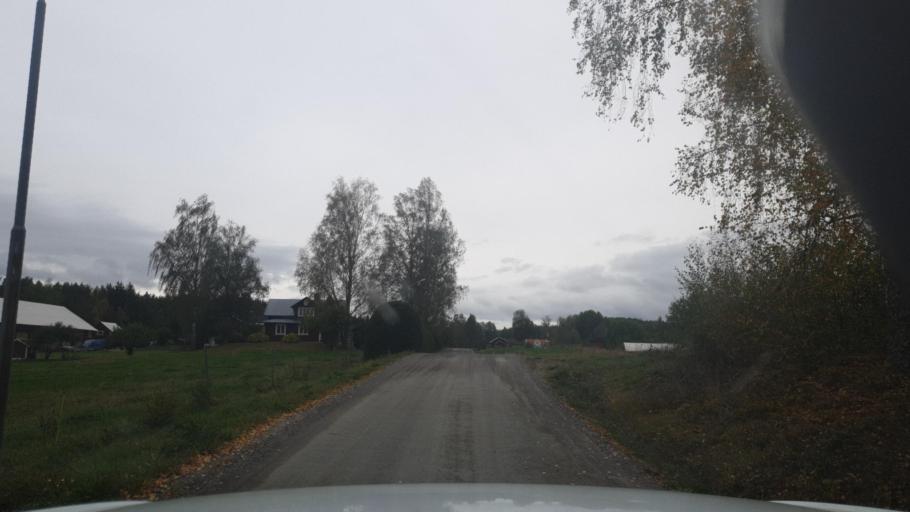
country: SE
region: Vaermland
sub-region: Karlstads Kommun
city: Edsvalla
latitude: 59.6133
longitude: 13.0671
